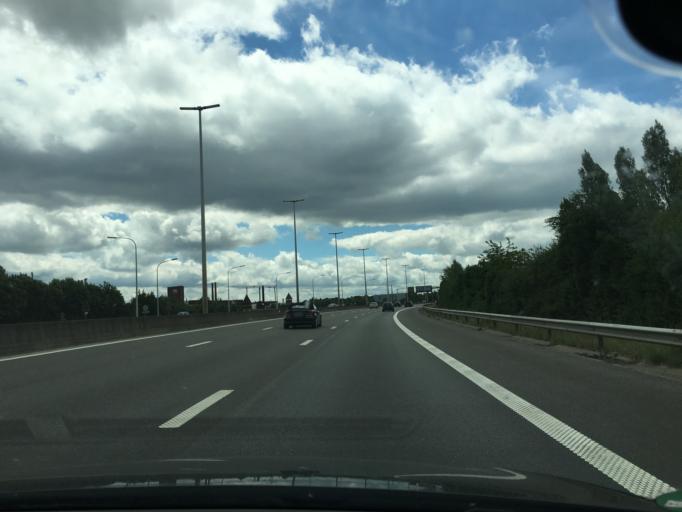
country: BE
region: Wallonia
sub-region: Province de Liege
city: Awans
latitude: 50.6576
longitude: 5.4871
